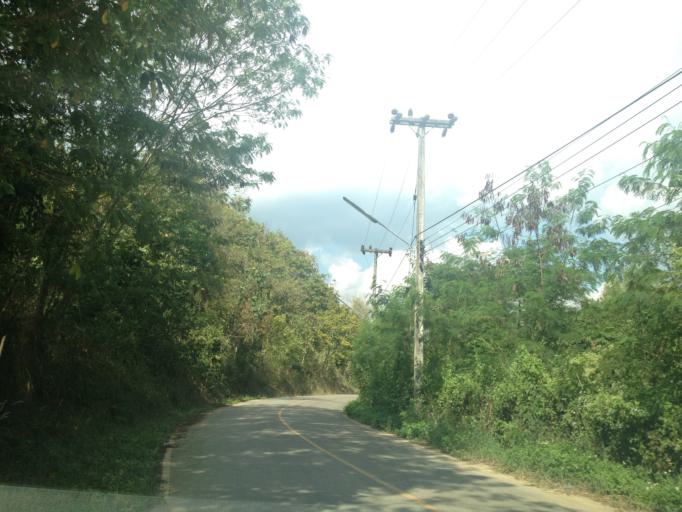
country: TH
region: Chiang Mai
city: Hang Dong
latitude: 18.7208
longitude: 98.8858
